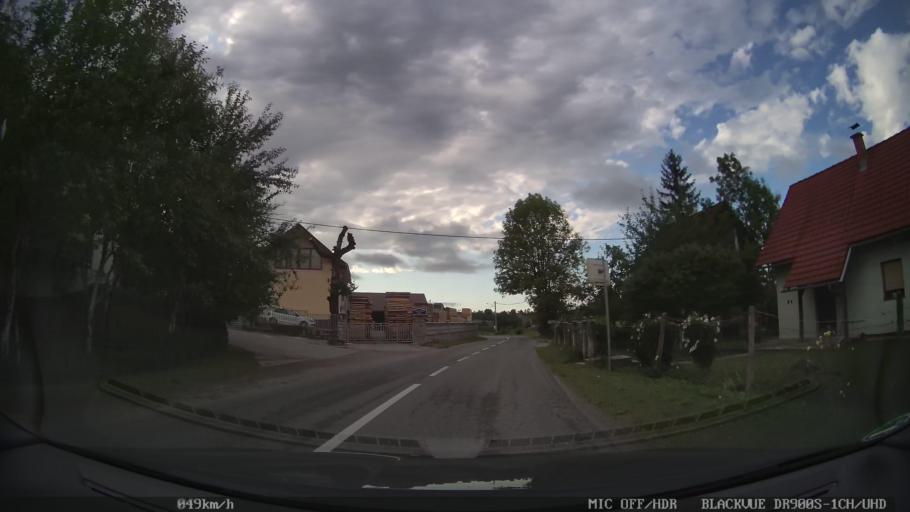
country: HR
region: Karlovacka
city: Plaski
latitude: 44.9848
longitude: 15.4724
